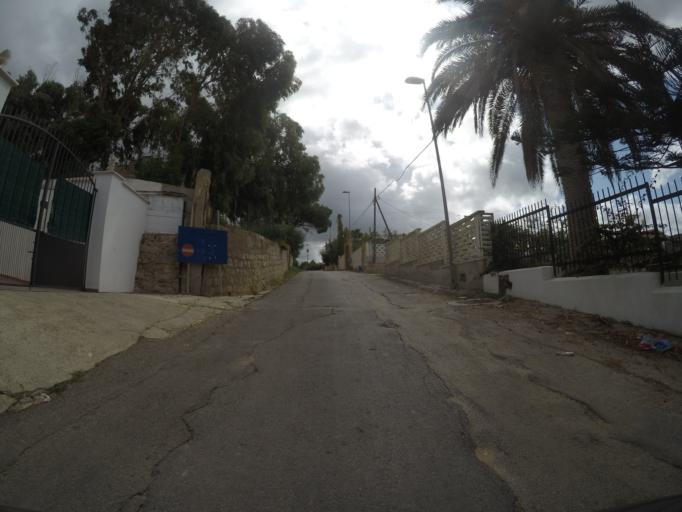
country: IT
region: Sicily
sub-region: Palermo
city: Trappeto
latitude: 38.0717
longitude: 13.0550
